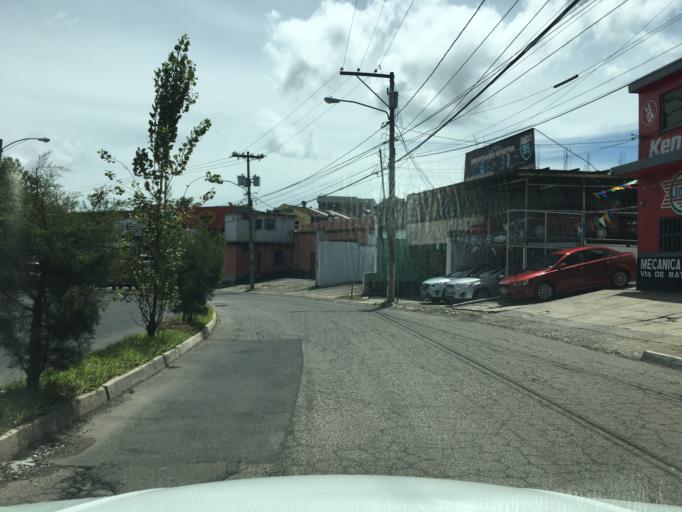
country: GT
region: Guatemala
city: Guatemala City
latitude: 14.6419
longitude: -90.5556
